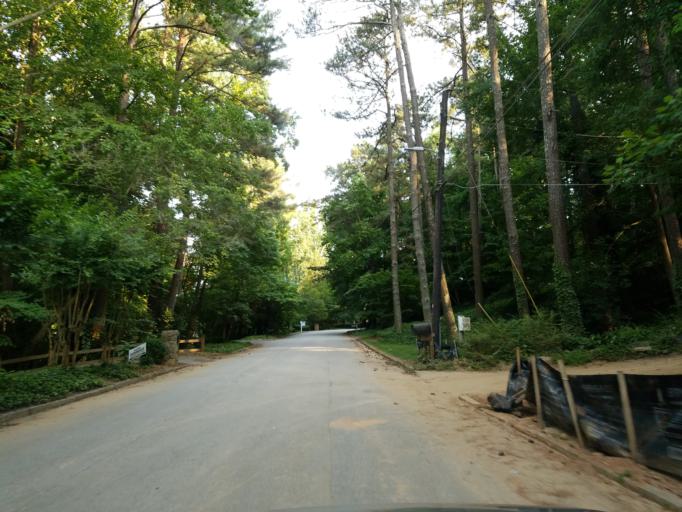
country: US
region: Georgia
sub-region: Cobb County
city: Vinings
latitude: 33.8542
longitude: -84.4345
